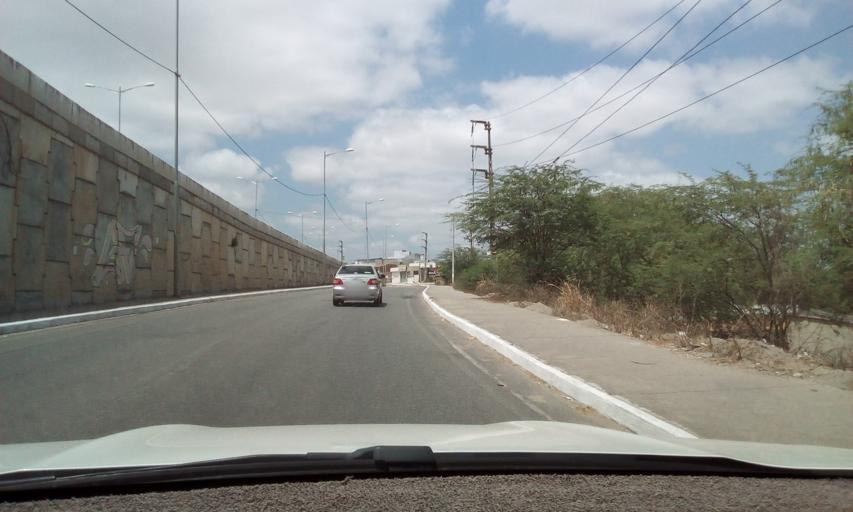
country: BR
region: Pernambuco
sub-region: Caruaru
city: Caruaru
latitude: -8.2828
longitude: -35.9819
